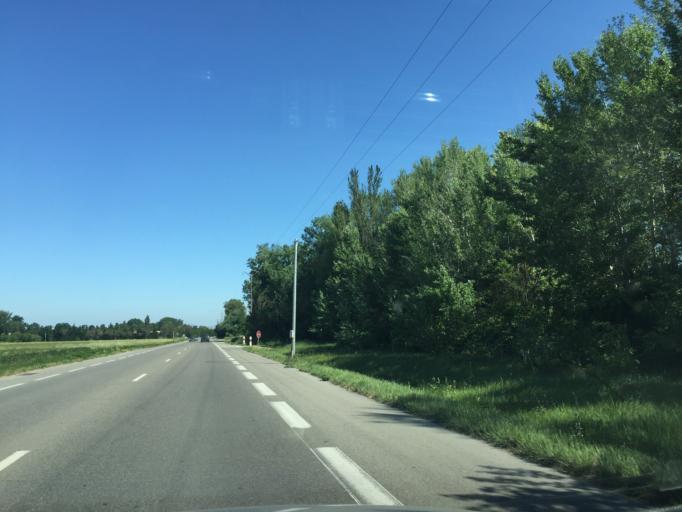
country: FR
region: Provence-Alpes-Cote d'Azur
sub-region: Departement du Vaucluse
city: Velleron
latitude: 43.9849
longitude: 5.0146
